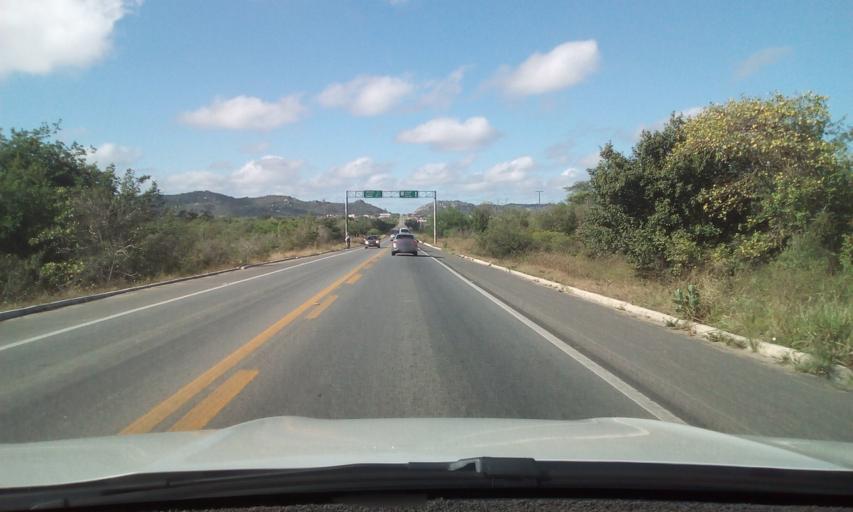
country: BR
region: Paraiba
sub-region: Campina Grande
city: Campina Grande
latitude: -7.3177
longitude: -35.8952
